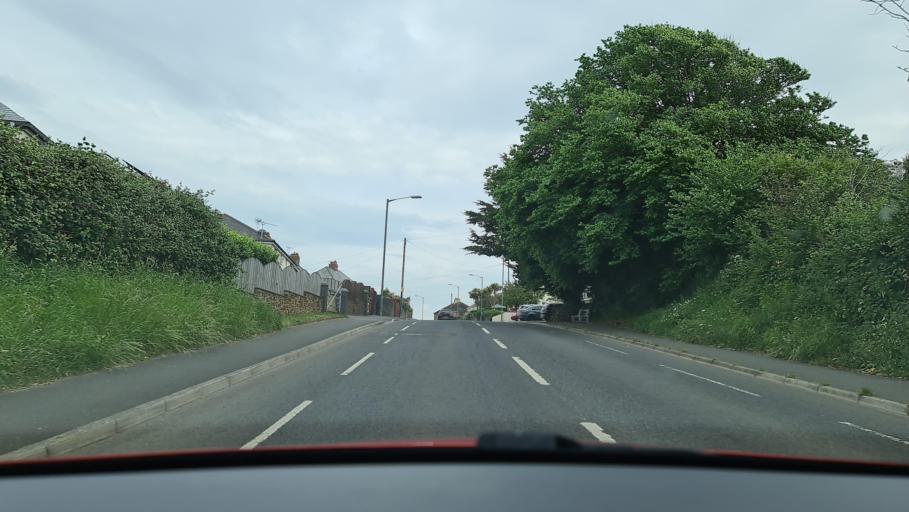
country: GB
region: England
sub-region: Cornwall
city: Bude
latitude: 50.8225
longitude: -4.5409
